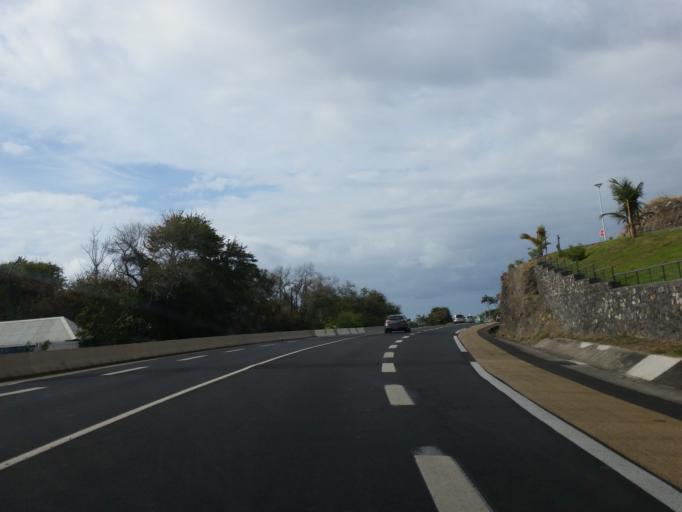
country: RE
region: Reunion
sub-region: Reunion
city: Saint-Paul
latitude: -21.0409
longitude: 55.2185
